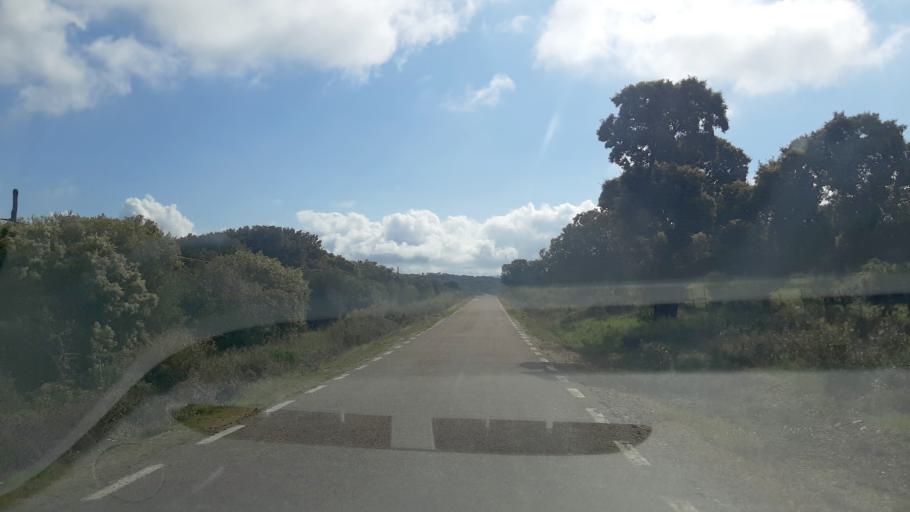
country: ES
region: Castille and Leon
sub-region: Provincia de Salamanca
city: Narros de Matalayegua
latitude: 40.7035
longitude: -5.9053
